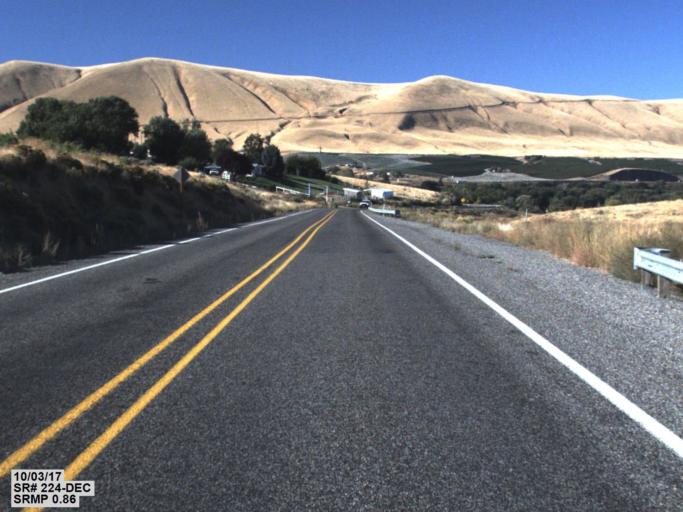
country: US
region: Washington
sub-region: Benton County
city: Benton City
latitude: 46.2615
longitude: -119.4625
